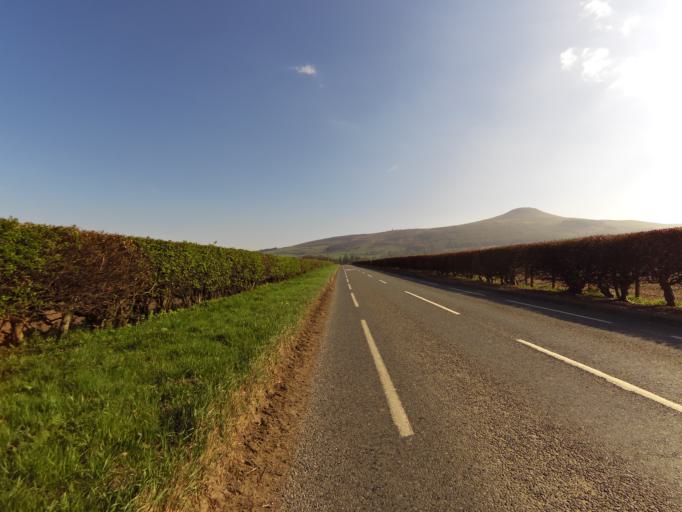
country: GB
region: Scotland
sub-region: Fife
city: Falkland
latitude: 56.2633
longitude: -3.2085
